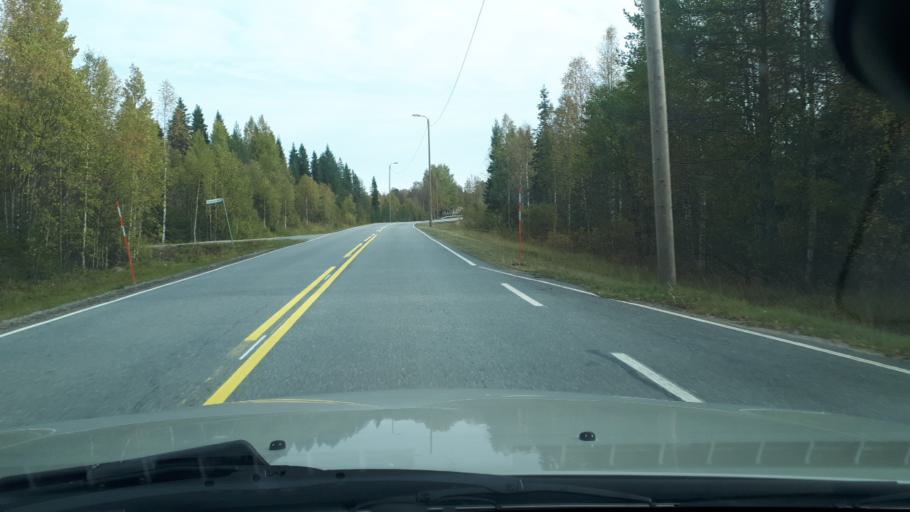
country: FI
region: Lapland
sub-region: Rovaniemi
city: Ranua
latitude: 66.0003
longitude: 26.2199
